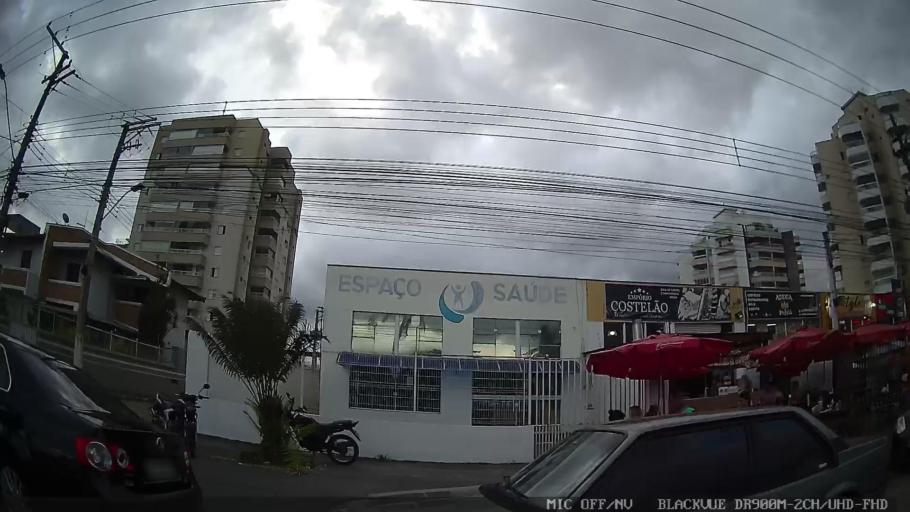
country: BR
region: Sao Paulo
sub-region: Caraguatatuba
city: Caraguatatuba
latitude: -23.6397
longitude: -45.4226
